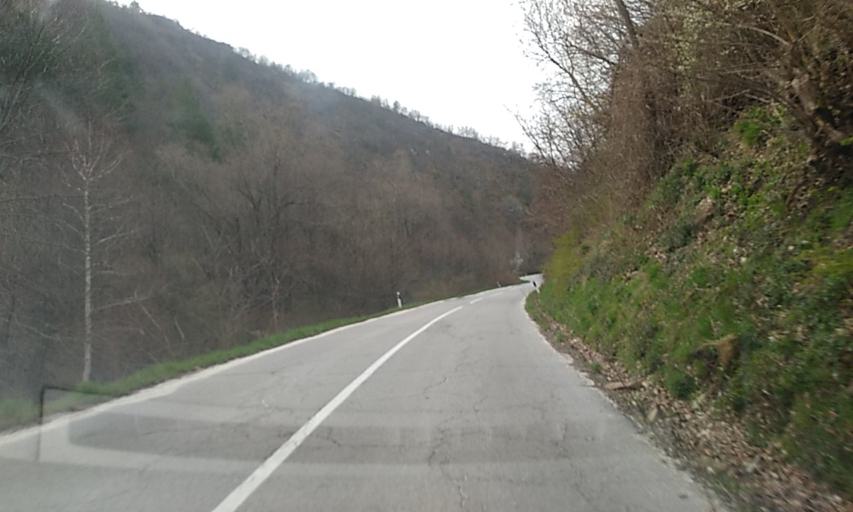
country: RS
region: Central Serbia
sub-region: Pcinjski Okrug
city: Bosilegrad
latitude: 42.5159
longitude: 22.4497
